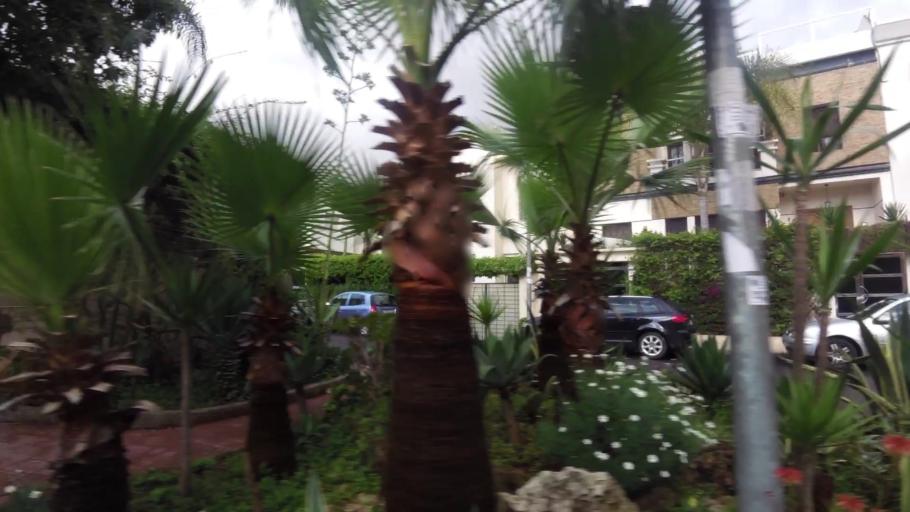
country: MA
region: Grand Casablanca
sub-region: Casablanca
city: Casablanca
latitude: 33.5468
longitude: -7.6601
